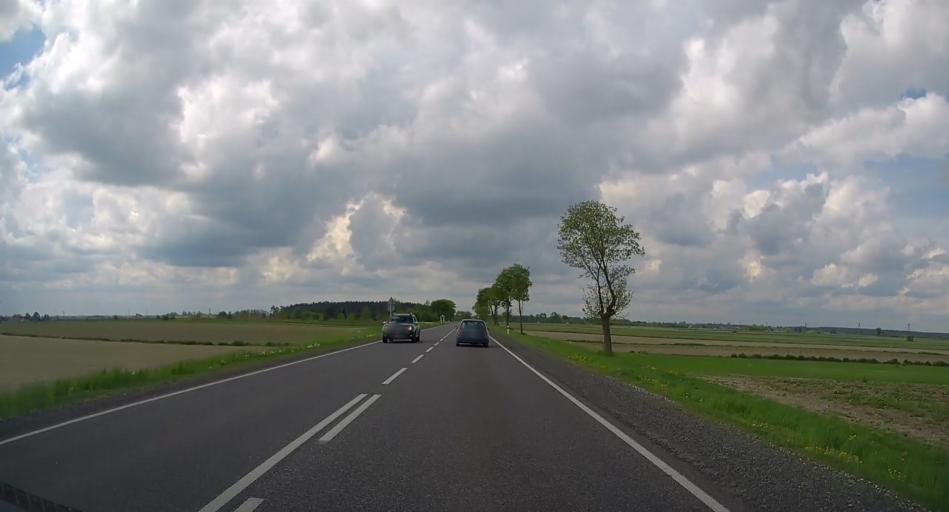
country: PL
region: Masovian Voivodeship
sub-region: Powiat nowodworski
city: Zakroczym
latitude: 52.4418
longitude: 20.5687
